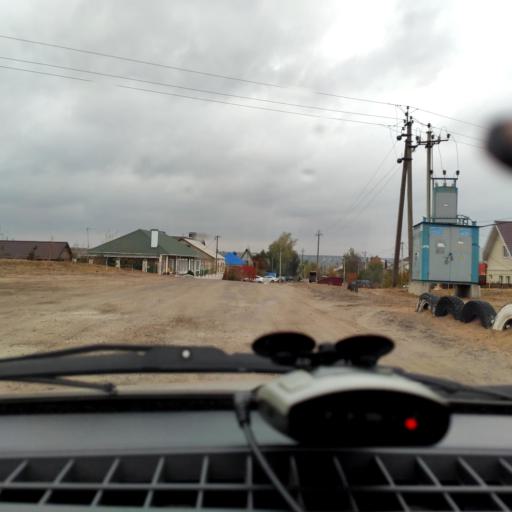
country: RU
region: Voronezj
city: Pridonskoy
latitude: 51.7006
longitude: 39.0729
